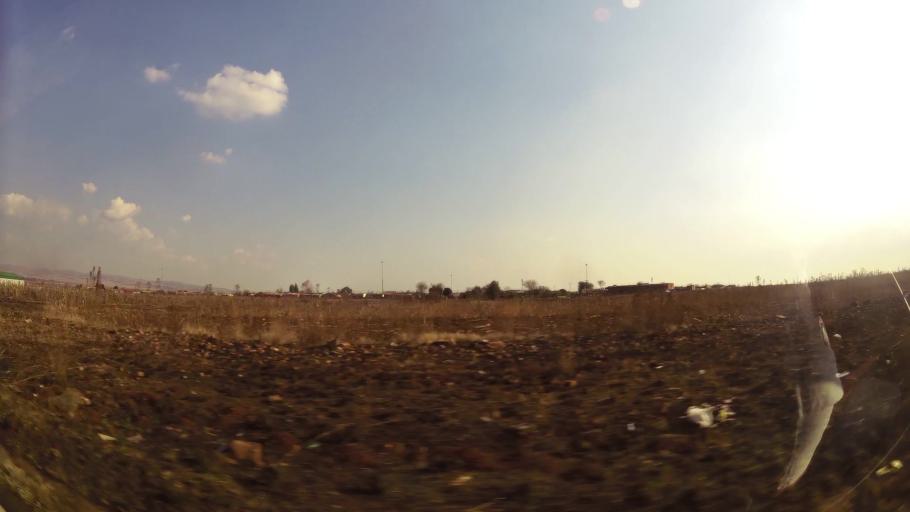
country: ZA
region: Gauteng
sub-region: Ekurhuleni Metropolitan Municipality
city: Germiston
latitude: -26.3724
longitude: 28.2084
